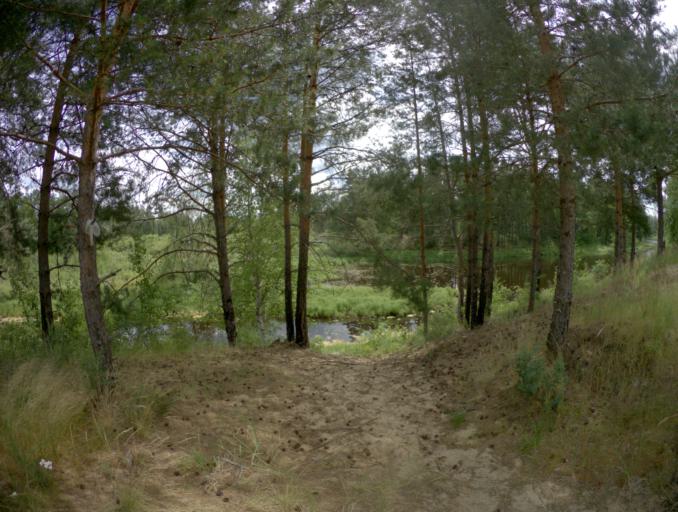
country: RU
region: Nizjnij Novgorod
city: Frolishchi
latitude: 56.4918
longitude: 42.5750
